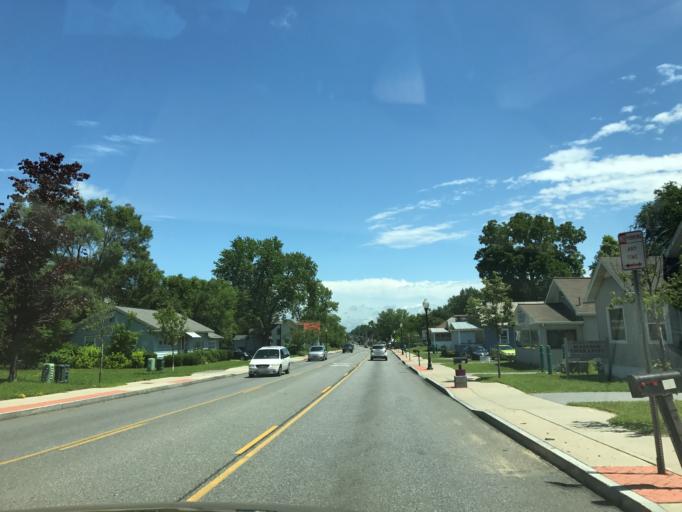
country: US
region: New York
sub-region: Warren County
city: West Glens Falls
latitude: 43.3008
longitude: -73.6674
